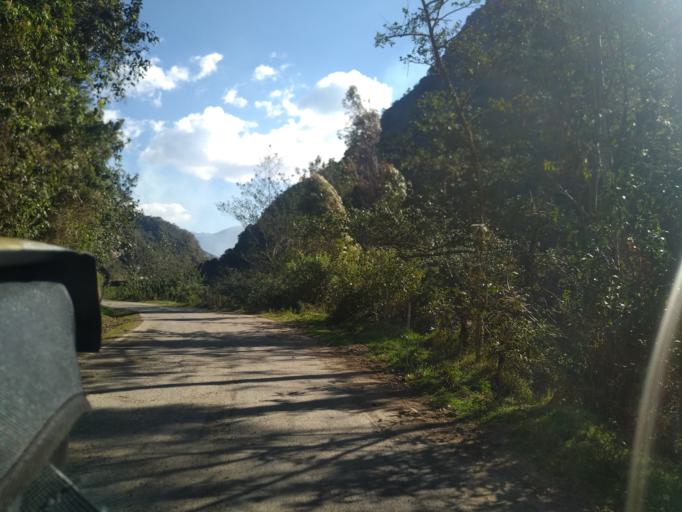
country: PE
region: Amazonas
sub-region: Provincia de Chachapoyas
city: Montevideo
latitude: -6.7206
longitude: -77.8235
